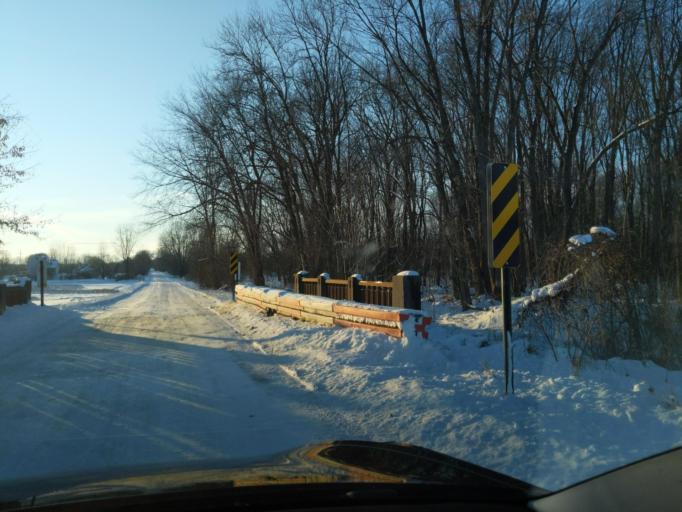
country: US
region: Michigan
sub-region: Livingston County
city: Fowlerville
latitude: 42.5680
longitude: -84.1252
